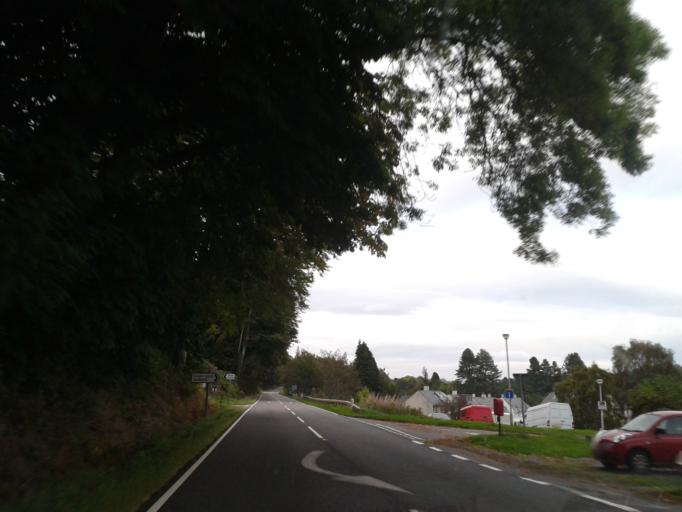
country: GB
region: Scotland
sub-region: Highland
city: Inverness
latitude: 57.4087
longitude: -4.3388
